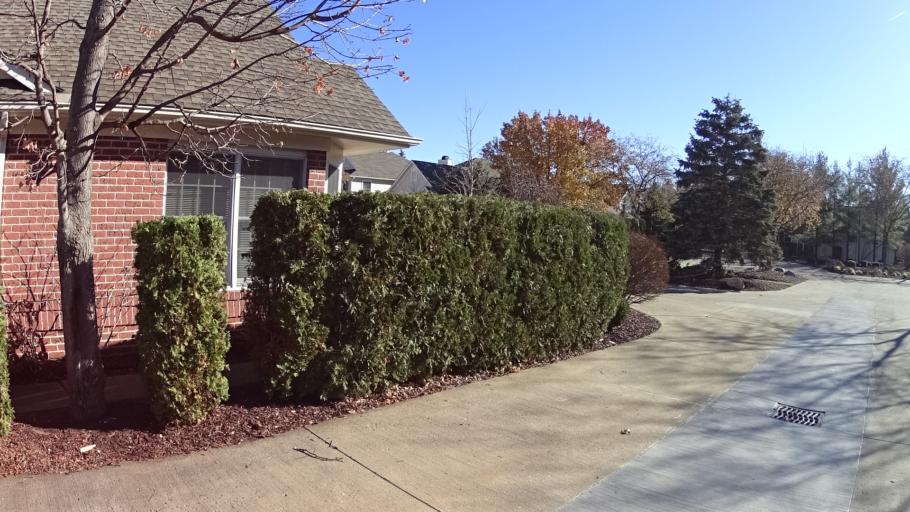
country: US
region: Ohio
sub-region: Lorain County
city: Avon Lake
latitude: 41.4952
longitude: -81.9787
